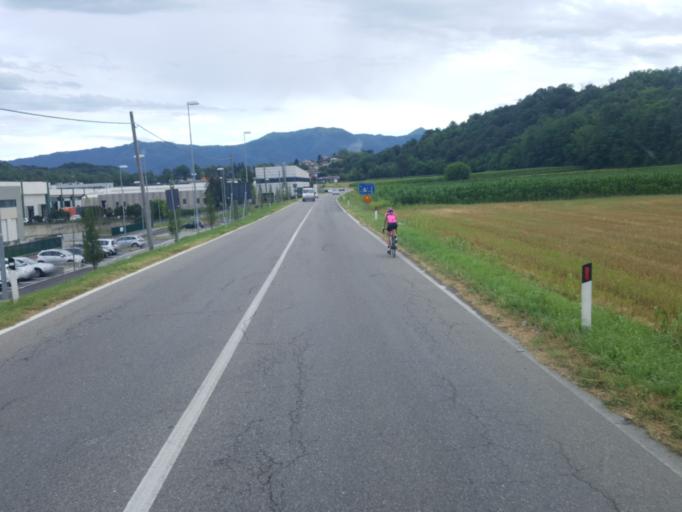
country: IT
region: Lombardy
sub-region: Provincia di Como
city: Brenna
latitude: 45.7369
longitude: 9.1983
